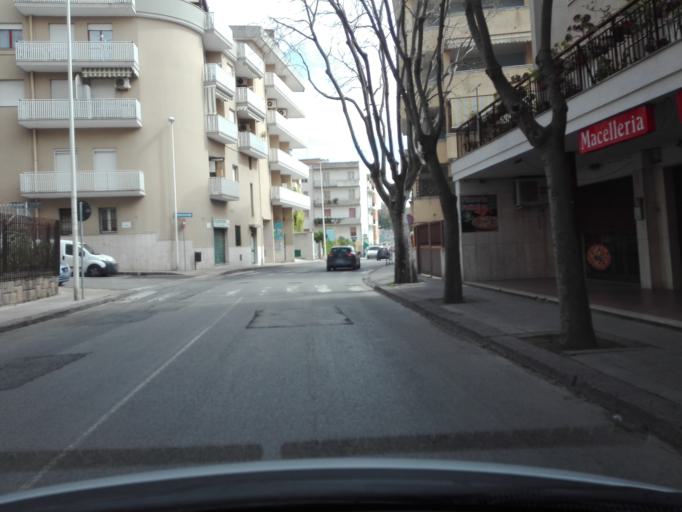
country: IT
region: Sardinia
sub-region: Provincia di Sassari
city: Sassari
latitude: 40.7341
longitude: 8.5691
